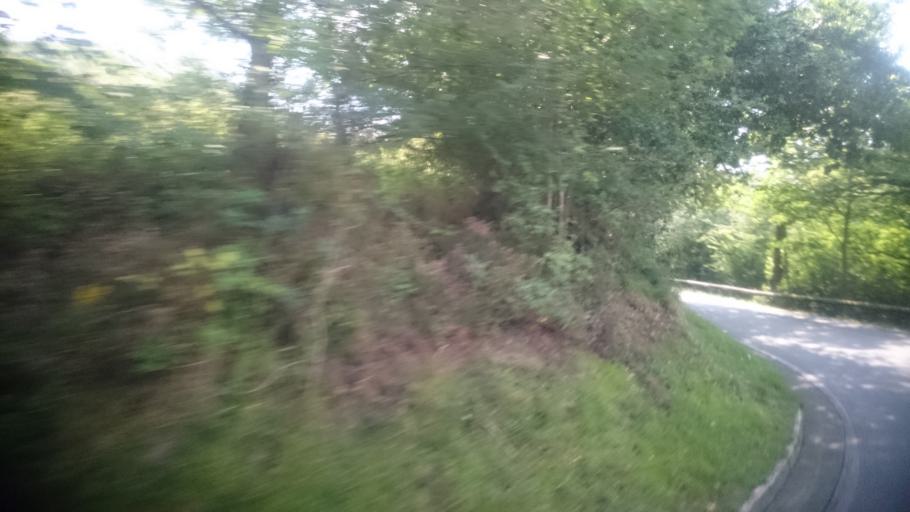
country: ES
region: Asturias
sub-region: Province of Asturias
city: Amieva
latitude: 43.3050
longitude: -5.0435
